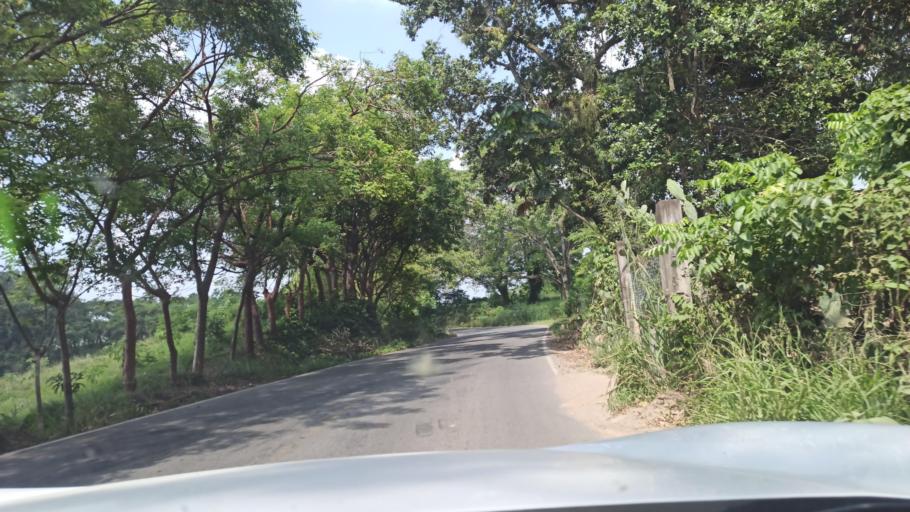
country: MX
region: Veracruz
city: Martinez de la Torre
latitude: 20.0826
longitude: -97.0716
